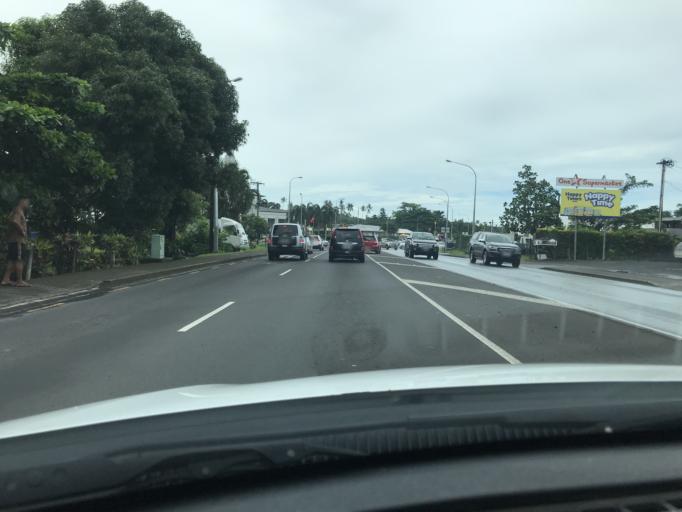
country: WS
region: Tuamasaga
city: Apia
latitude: -13.8378
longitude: -171.7813
